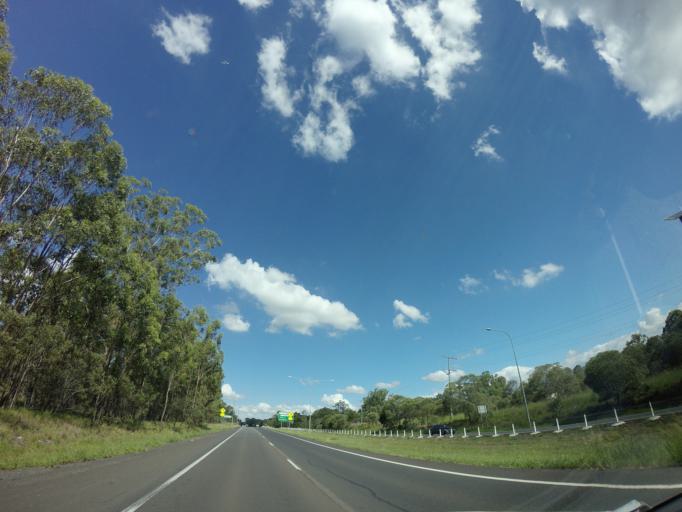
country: AU
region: Queensland
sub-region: Ipswich
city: Thagoona
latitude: -27.5749
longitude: 152.6626
